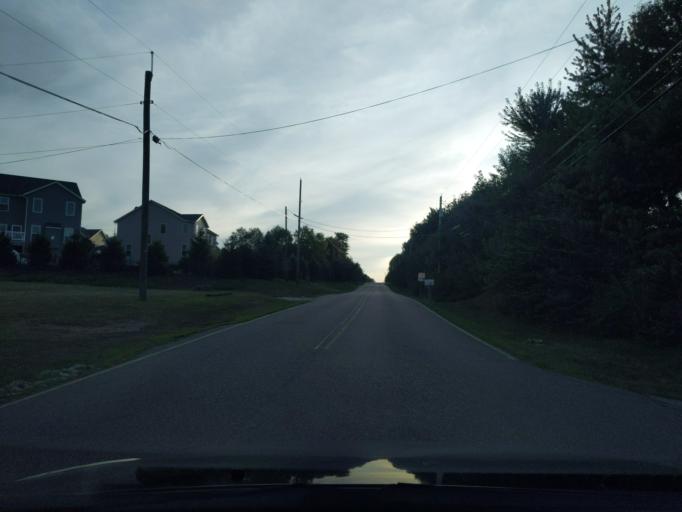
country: US
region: Ohio
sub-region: Stark County
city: Greentown
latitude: 40.9145
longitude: -81.3903
